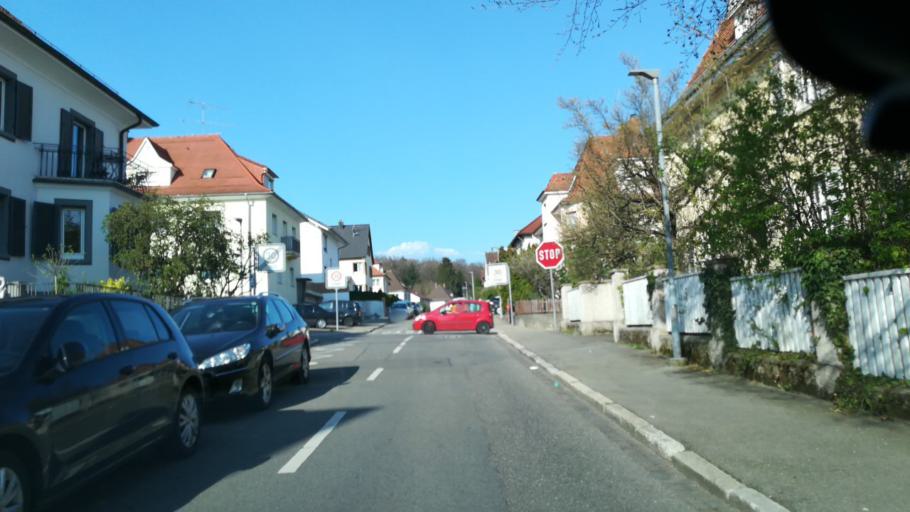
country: DE
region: Baden-Wuerttemberg
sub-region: Freiburg Region
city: Singen
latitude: 47.7661
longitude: 8.8456
